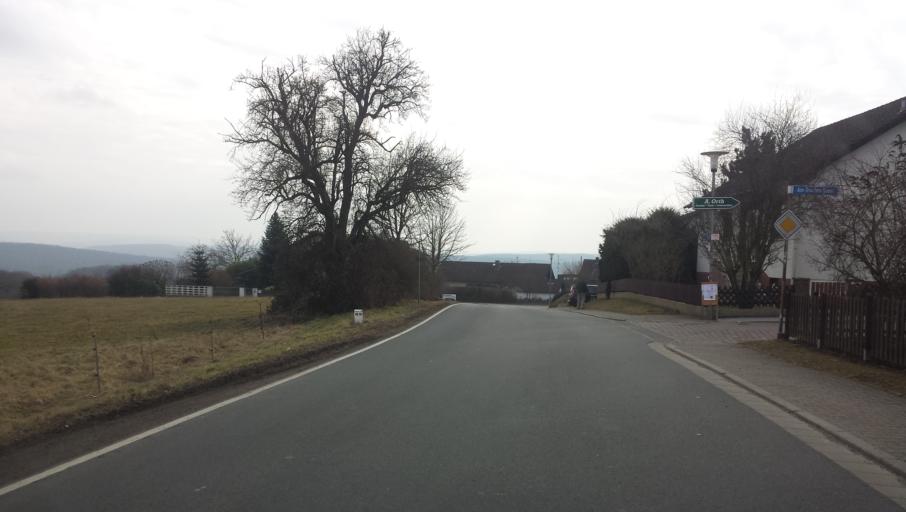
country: DE
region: Hesse
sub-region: Regierungsbezirk Darmstadt
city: Brensbach
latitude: 49.7824
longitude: 8.9385
